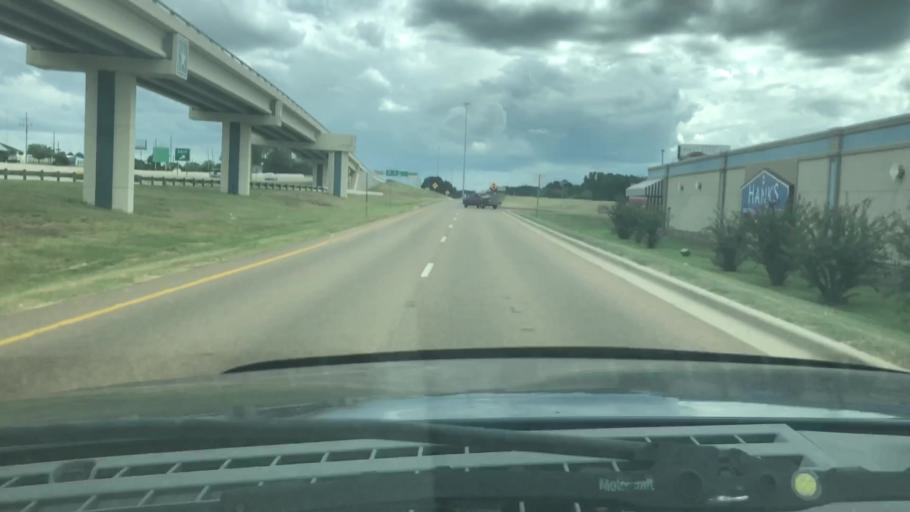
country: US
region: Texas
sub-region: Bowie County
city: Wake Village
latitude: 33.4474
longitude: -94.0973
